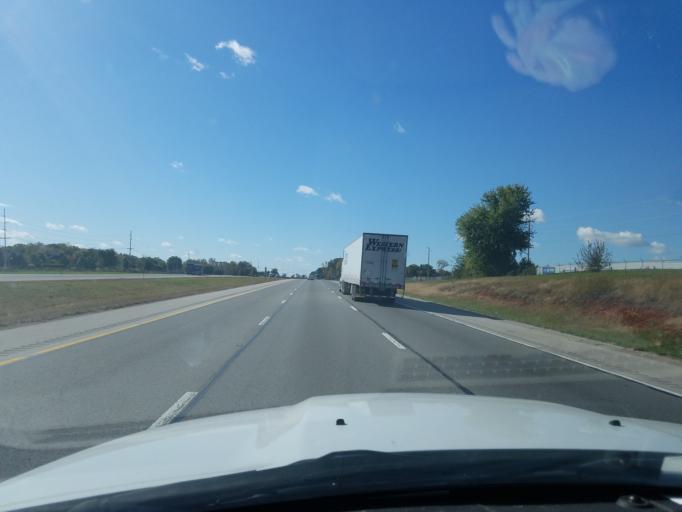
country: US
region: Kentucky
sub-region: Warren County
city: Bowling Green
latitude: 36.9561
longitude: -86.4044
